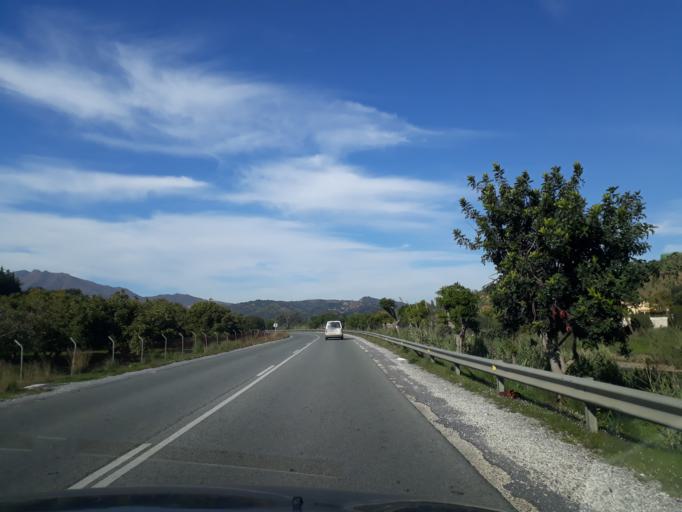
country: ES
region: Andalusia
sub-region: Provincia de Malaga
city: Fuengirola
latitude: 36.5456
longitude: -4.6886
